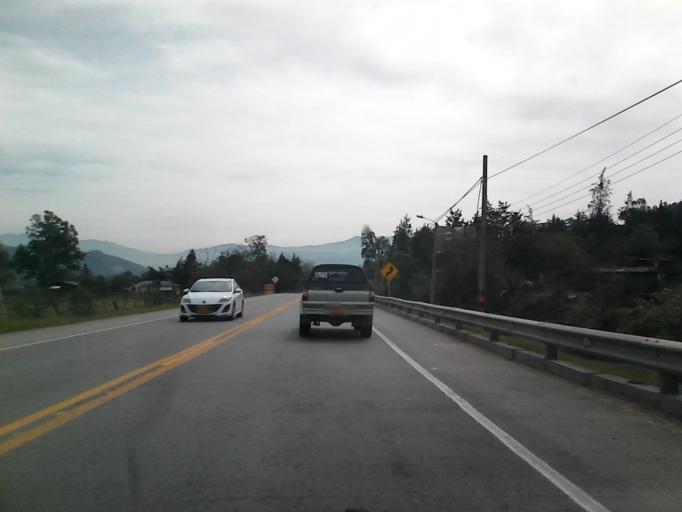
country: CO
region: Boyaca
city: Tibasosa
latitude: 5.7446
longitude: -72.9877
